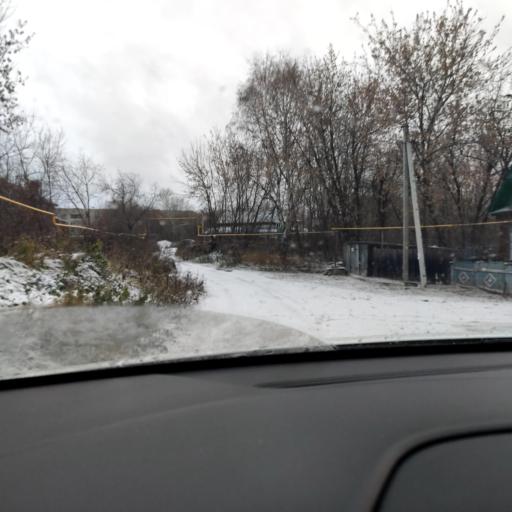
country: RU
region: Tatarstan
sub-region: Gorod Kazan'
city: Kazan
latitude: 55.8101
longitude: 49.0851
